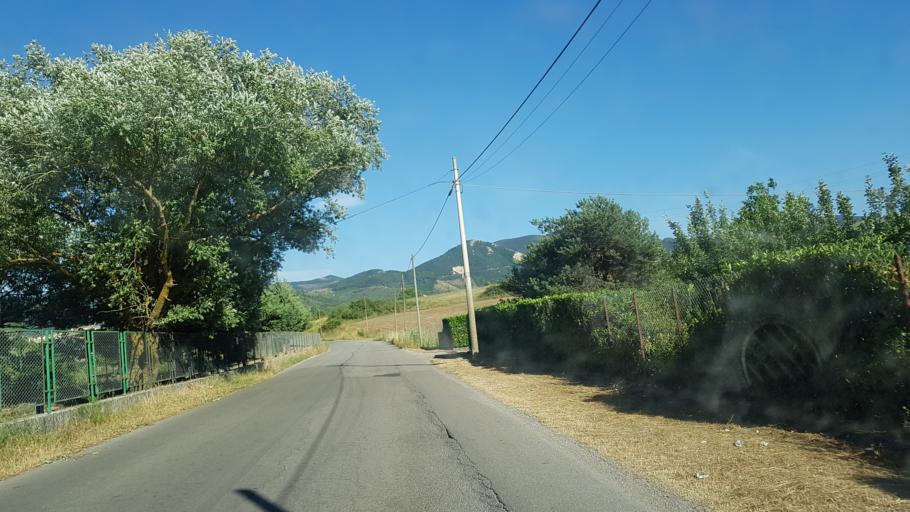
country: IT
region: Basilicate
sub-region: Provincia di Potenza
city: Pignola
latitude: 40.5793
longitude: 15.7465
